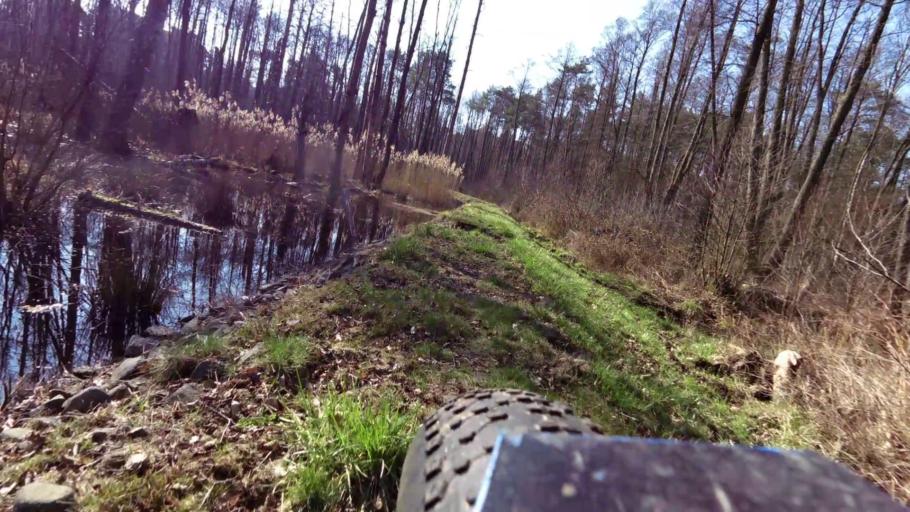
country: PL
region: Lubusz
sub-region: Powiat krosnienski
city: Maszewo
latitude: 52.2127
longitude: 14.9529
